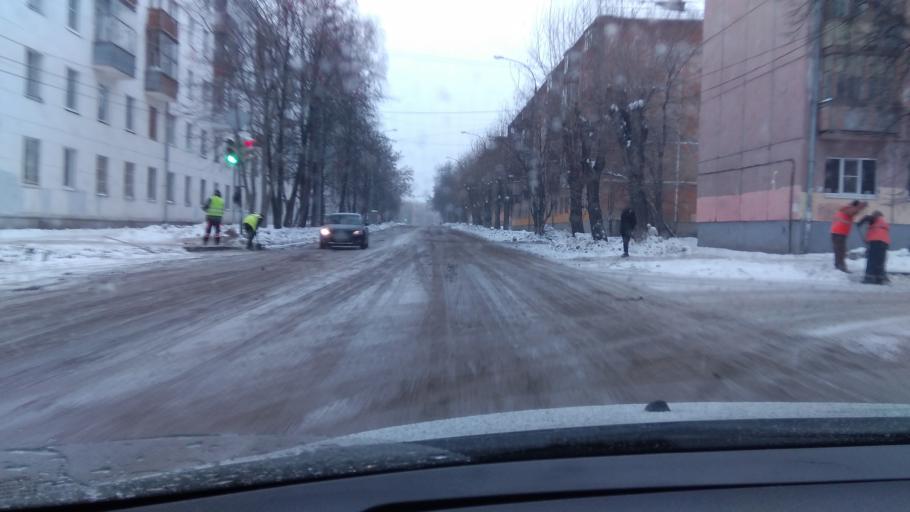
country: RU
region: Sverdlovsk
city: Yekaterinburg
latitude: 56.8899
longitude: 60.5808
